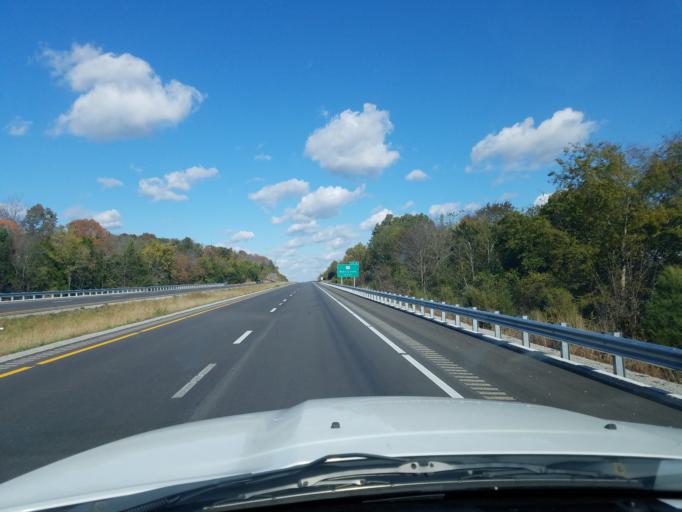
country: US
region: Kentucky
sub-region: Warren County
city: Bowling Green
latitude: 36.9638
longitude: -86.4982
